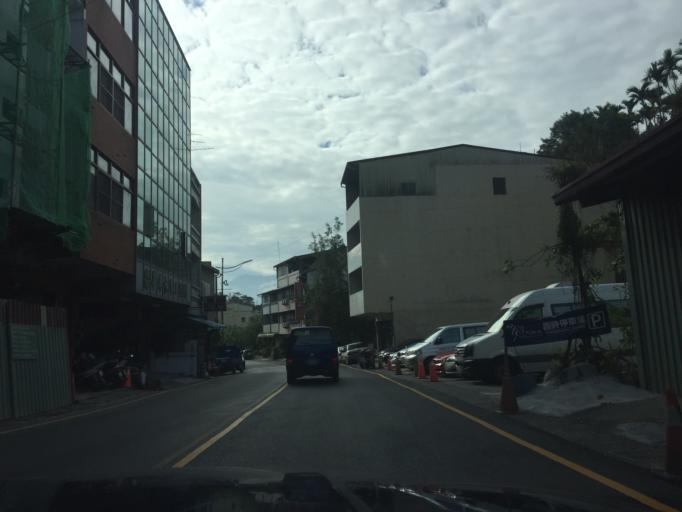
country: TW
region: Taiwan
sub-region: Nantou
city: Puli
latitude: 23.8660
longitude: 120.9028
